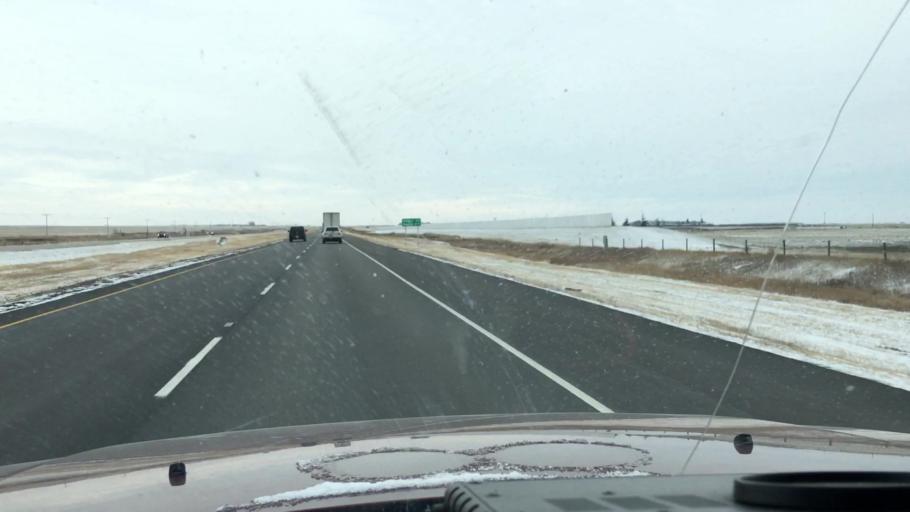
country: CA
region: Saskatchewan
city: Saskatoon
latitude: 51.8080
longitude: -106.4945
